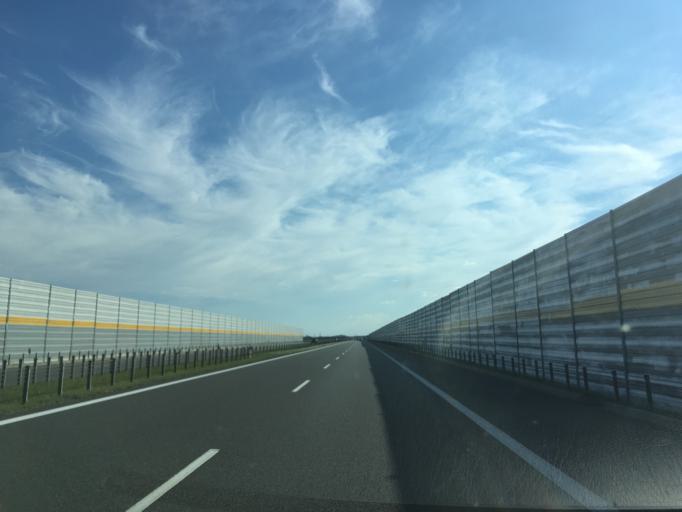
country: PL
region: Kujawsko-Pomorskie
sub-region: Powiat chelminski
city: Lisewo
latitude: 53.3077
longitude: 18.7061
